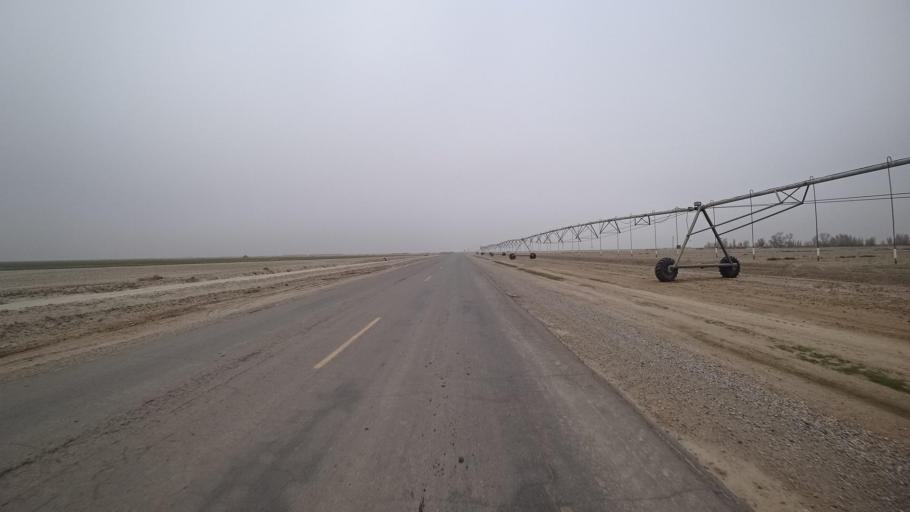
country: US
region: California
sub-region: Kern County
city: Rosedale
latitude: 35.2381
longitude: -119.2399
